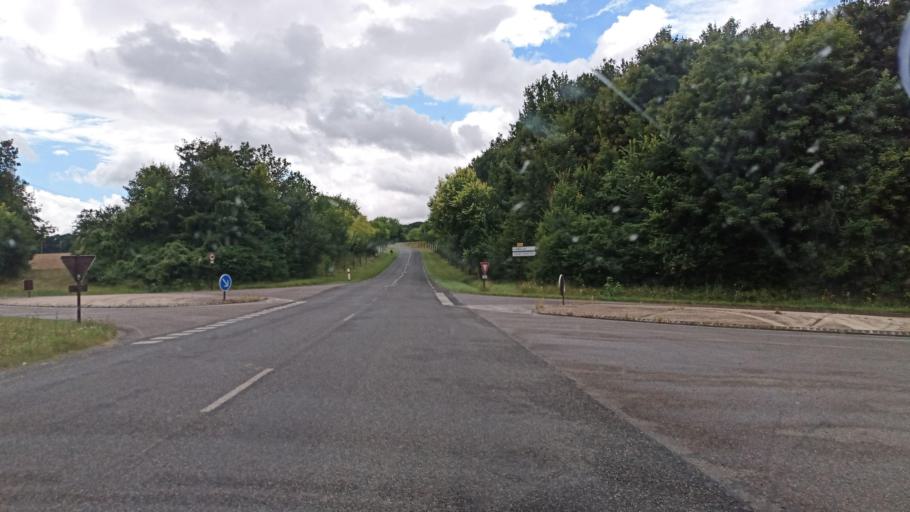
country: FR
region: Ile-de-France
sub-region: Departement de Seine-et-Marne
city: Voulx
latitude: 48.2843
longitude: 2.9564
